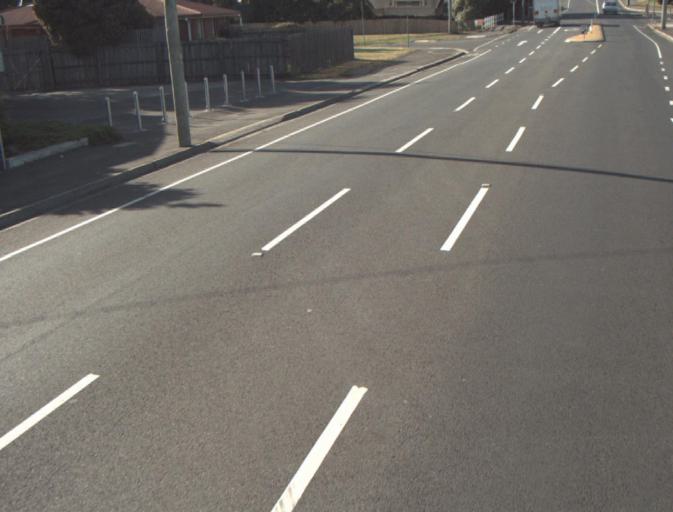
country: AU
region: Tasmania
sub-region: Launceston
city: Newnham
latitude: -41.3981
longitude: 147.1284
